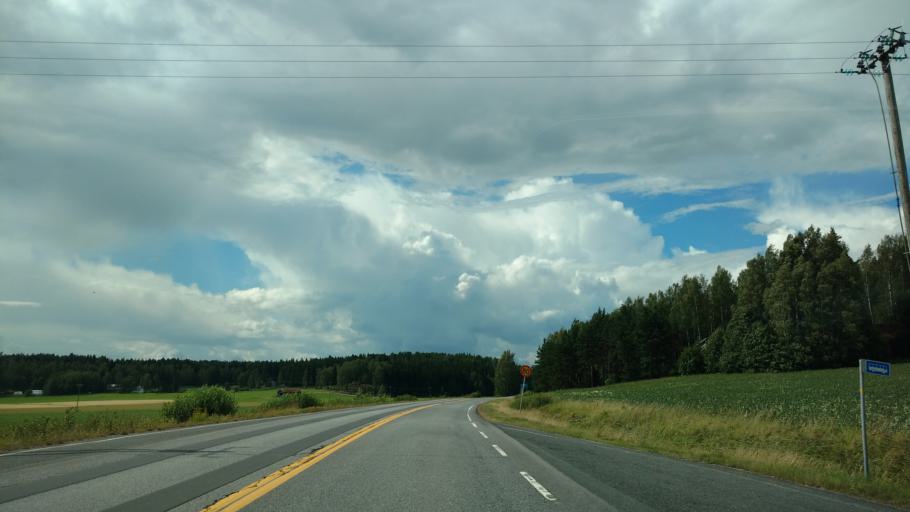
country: FI
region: Varsinais-Suomi
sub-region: Salo
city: Halikko
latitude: 60.3830
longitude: 22.8927
